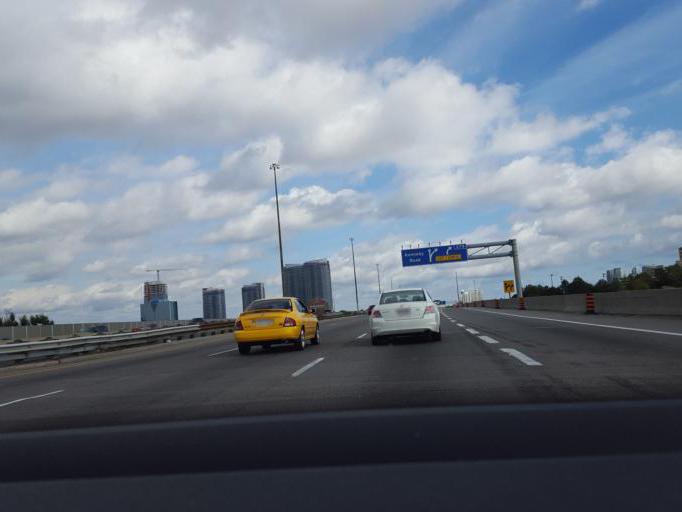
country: CA
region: Ontario
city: Scarborough
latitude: 43.7722
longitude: -79.2950
